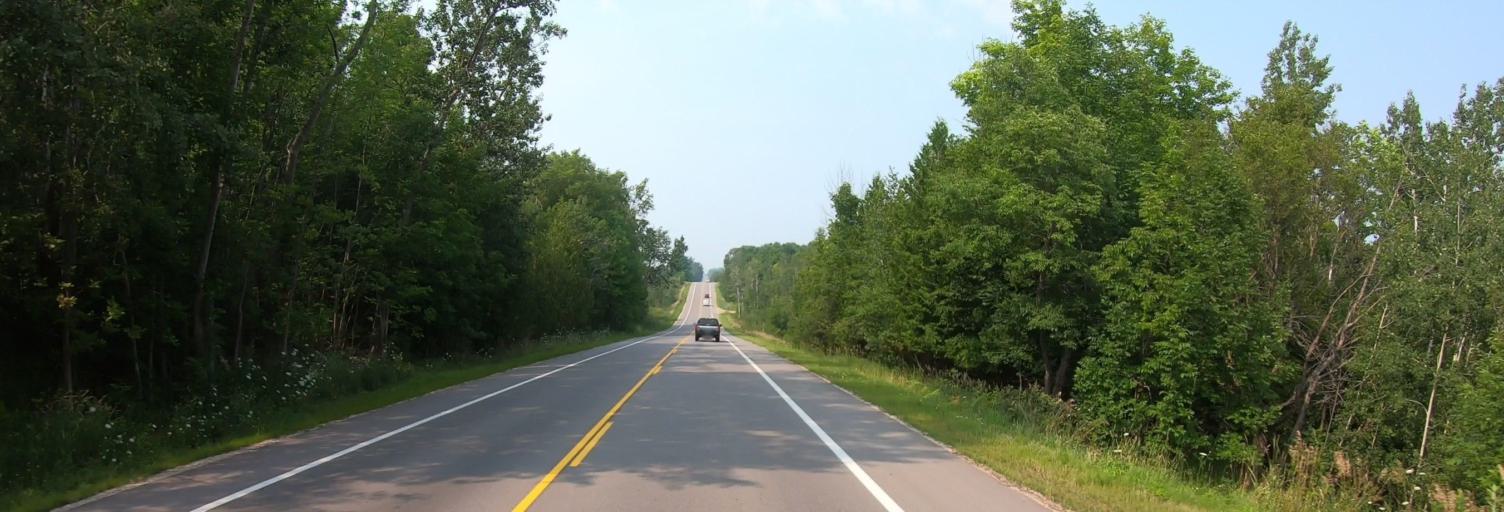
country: US
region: Michigan
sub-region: Charlevoix County
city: Charlevoix
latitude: 45.2261
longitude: -85.2613
